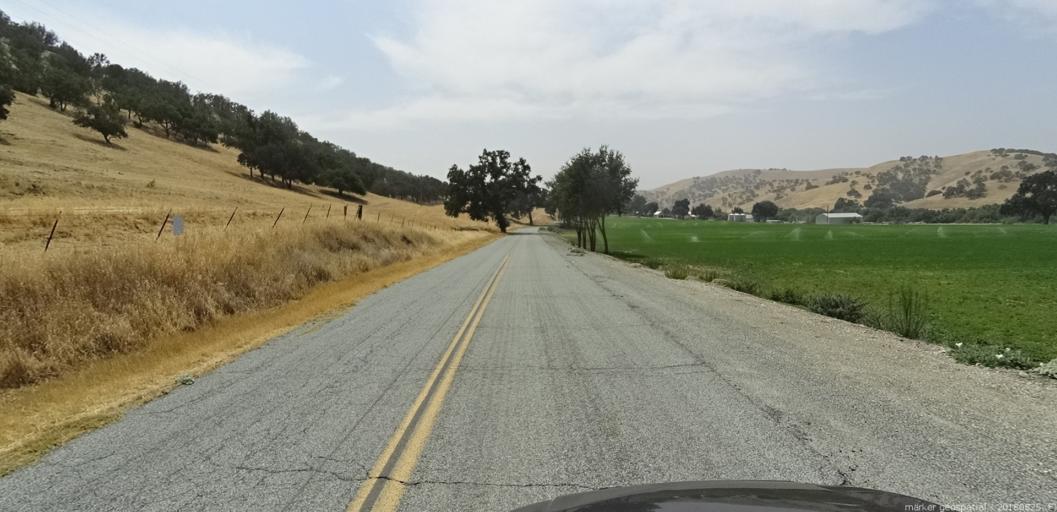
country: US
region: California
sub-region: San Luis Obispo County
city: San Miguel
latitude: 35.8136
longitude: -120.6674
